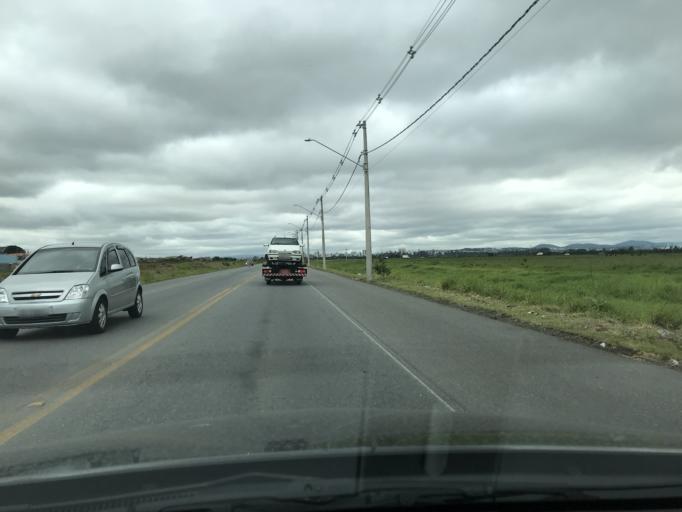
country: BR
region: Sao Paulo
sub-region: Itaquaquecetuba
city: Itaquaquecetuba
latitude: -23.4987
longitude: -46.3230
